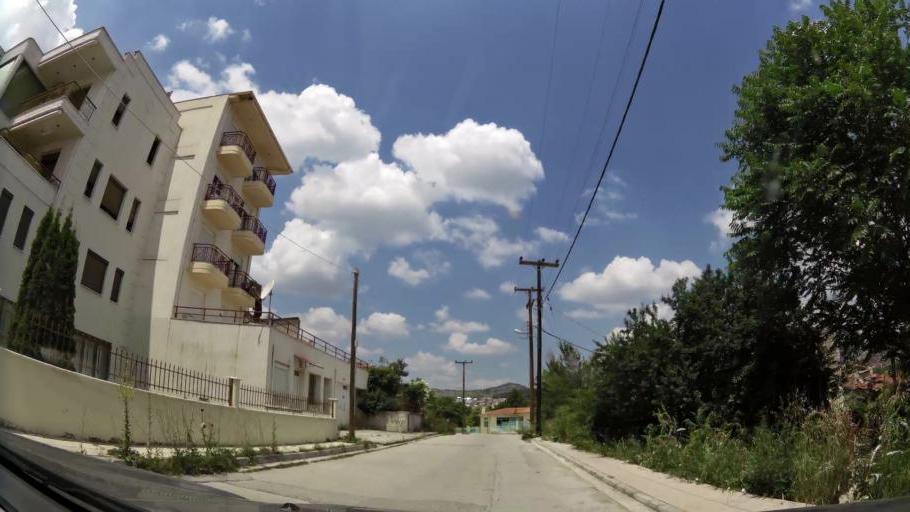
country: GR
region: West Macedonia
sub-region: Nomos Kozanis
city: Kozani
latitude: 40.2913
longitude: 21.7885
